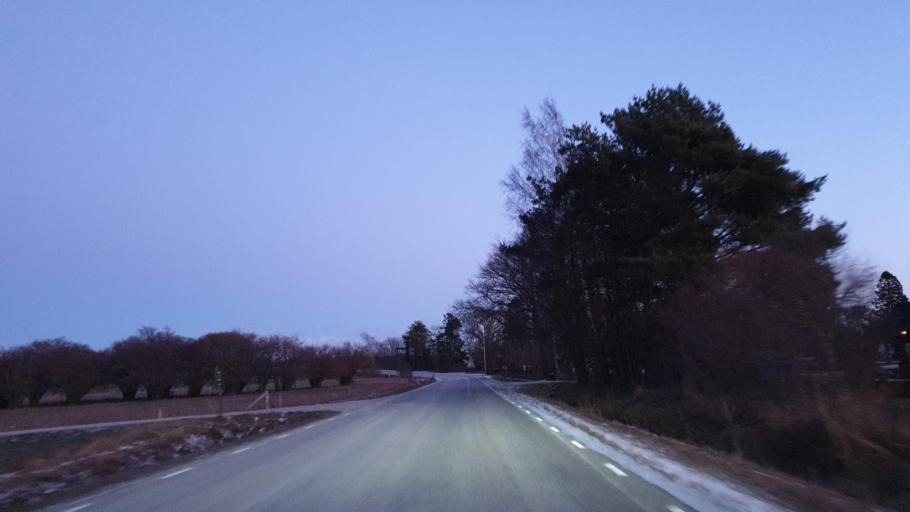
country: SE
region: Gotland
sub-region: Gotland
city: Slite
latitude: 57.4189
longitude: 18.8756
